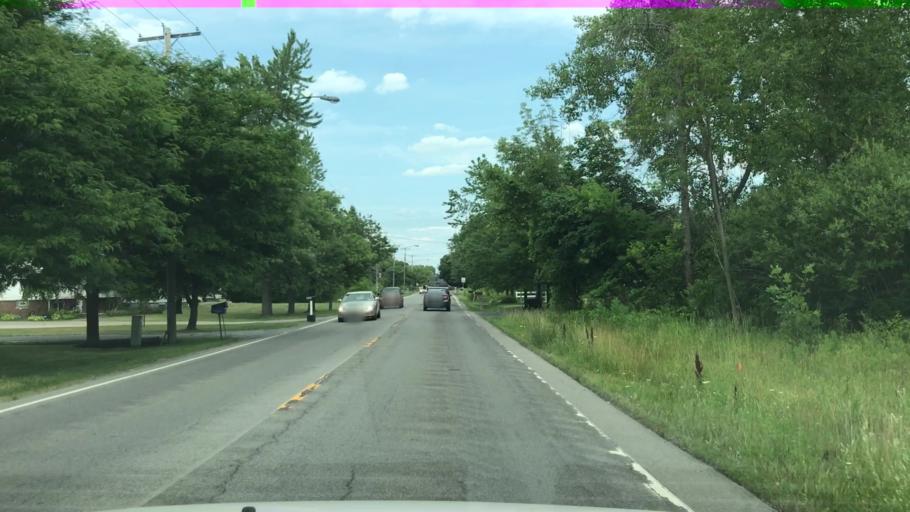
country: US
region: New York
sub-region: Erie County
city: Depew
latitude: 42.8805
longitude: -78.6849
